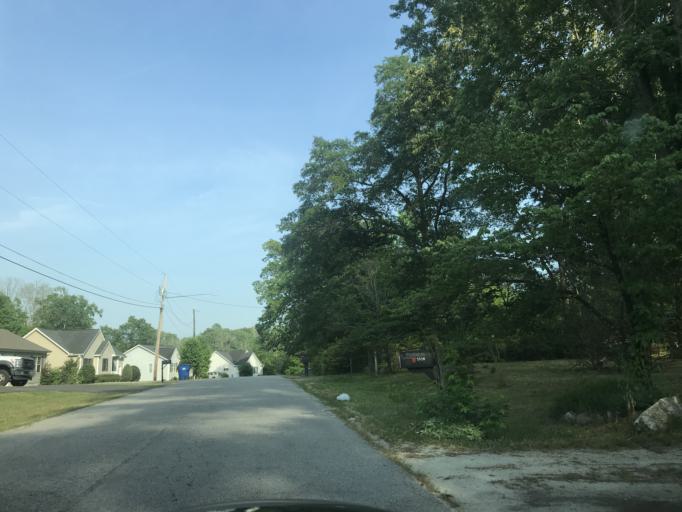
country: US
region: North Carolina
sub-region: Wake County
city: Garner
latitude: 35.7456
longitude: -78.5729
